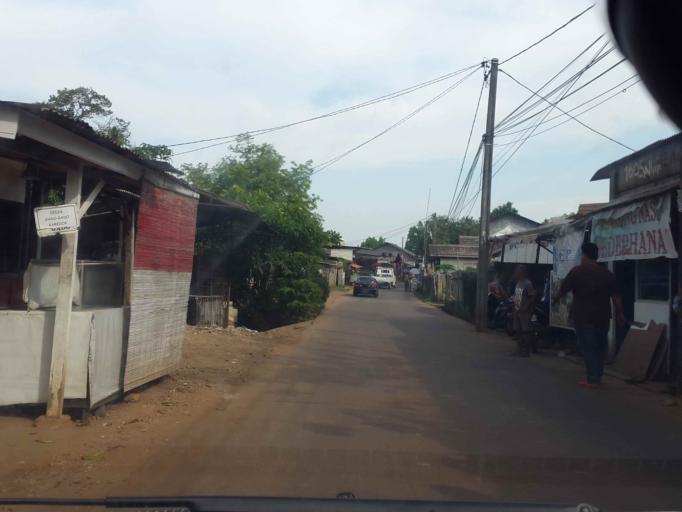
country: ID
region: West Java
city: Ciputat
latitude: -6.2561
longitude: 106.6743
